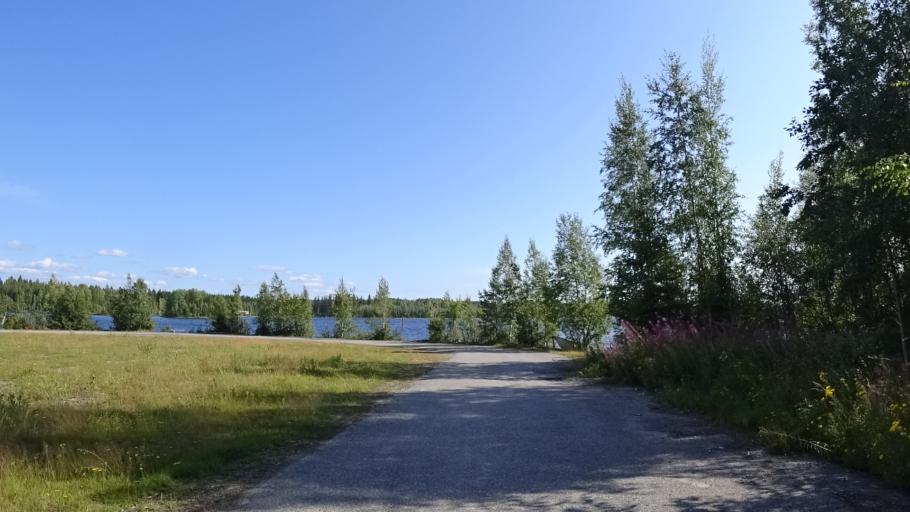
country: FI
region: North Karelia
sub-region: Joensuu
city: Eno
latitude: 62.8009
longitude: 30.1199
